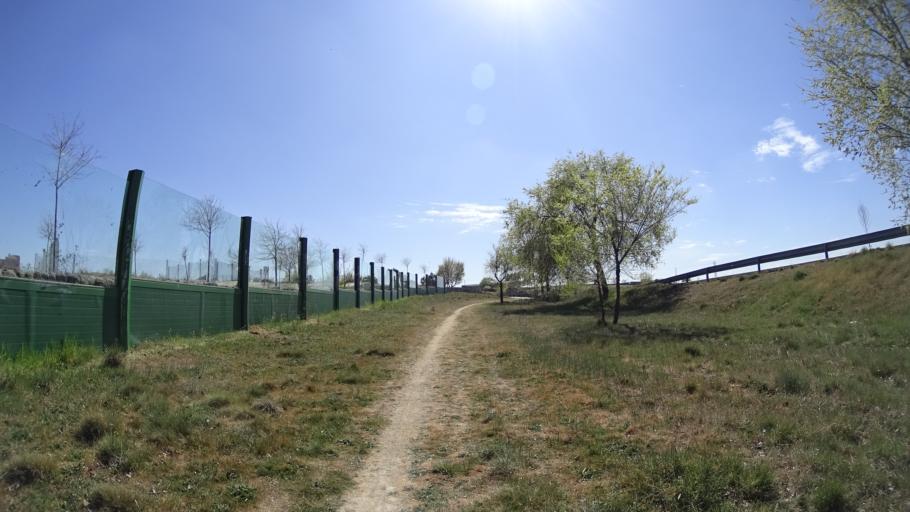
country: ES
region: Madrid
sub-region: Provincia de Madrid
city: Colmenar Viejo
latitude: 40.6495
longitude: -3.7925
